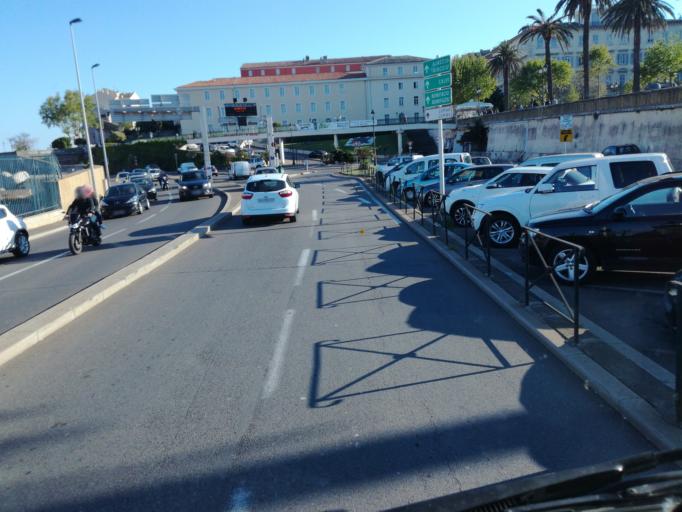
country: FR
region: Corsica
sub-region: Departement de la Haute-Corse
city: Bastia
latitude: 42.7005
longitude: 9.4520
